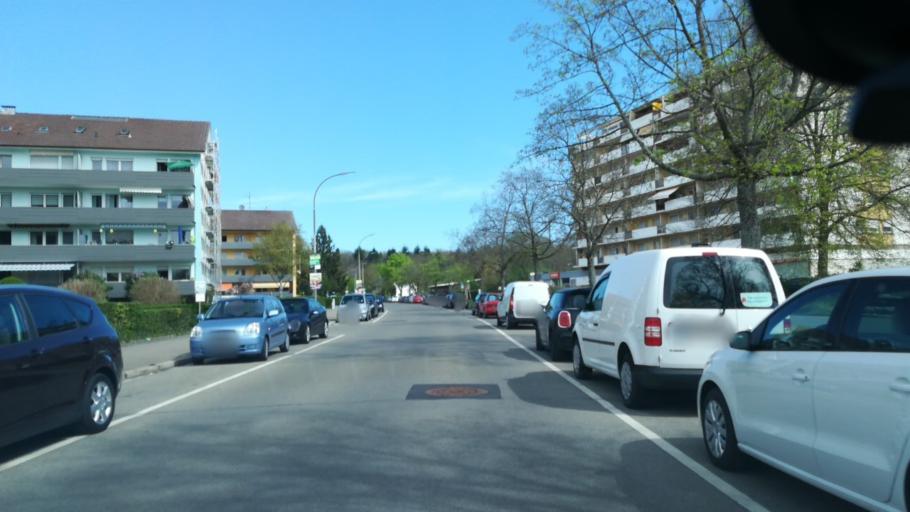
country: DE
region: Baden-Wuerttemberg
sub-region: Freiburg Region
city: Singen
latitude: 47.7726
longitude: 8.8452
